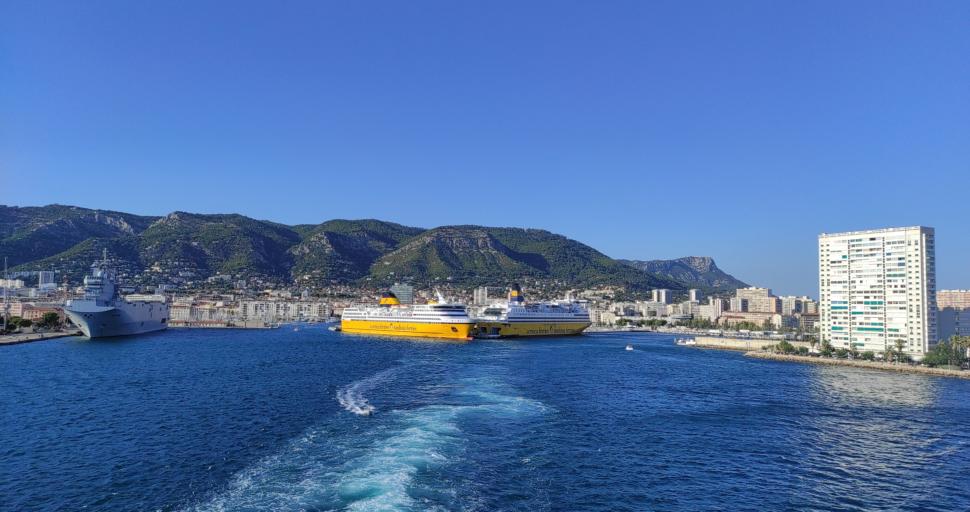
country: FR
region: Provence-Alpes-Cote d'Azur
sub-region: Departement du Var
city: Toulon
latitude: 43.1118
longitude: 5.9266
